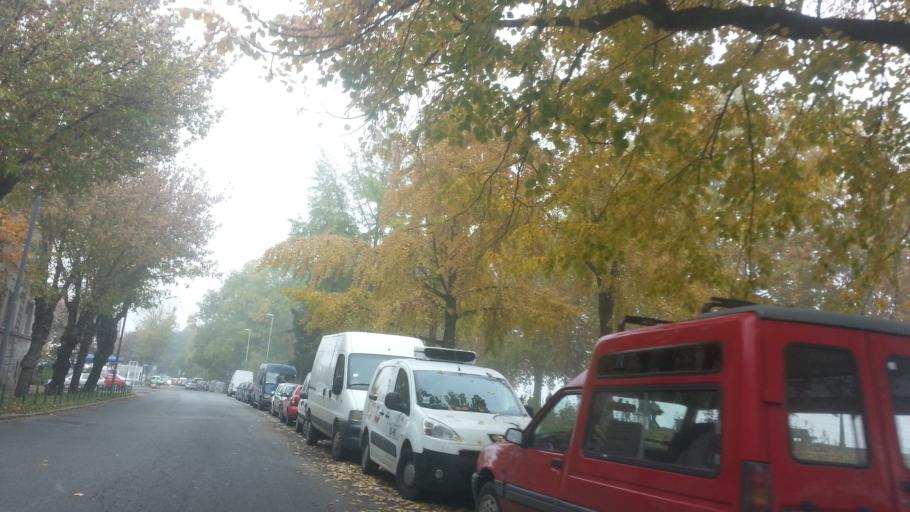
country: RS
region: Central Serbia
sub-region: Belgrade
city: Zemun
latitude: 44.8429
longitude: 20.4170
